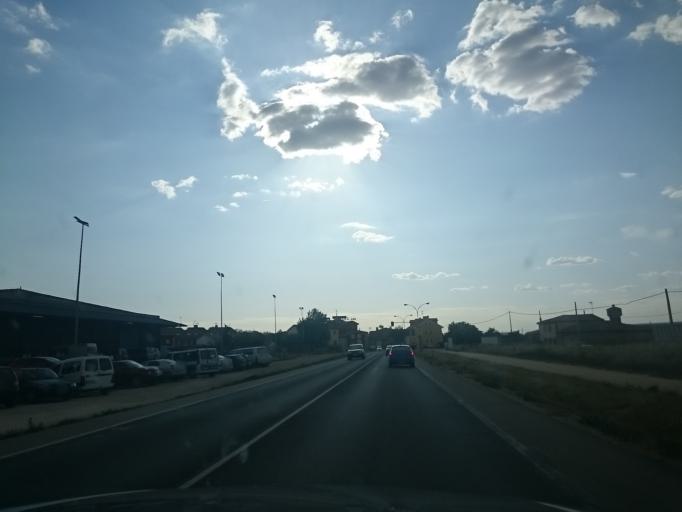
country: ES
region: Castille and Leon
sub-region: Provincia de Burgos
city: Cardenajimeno
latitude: 42.3435
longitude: -3.6236
